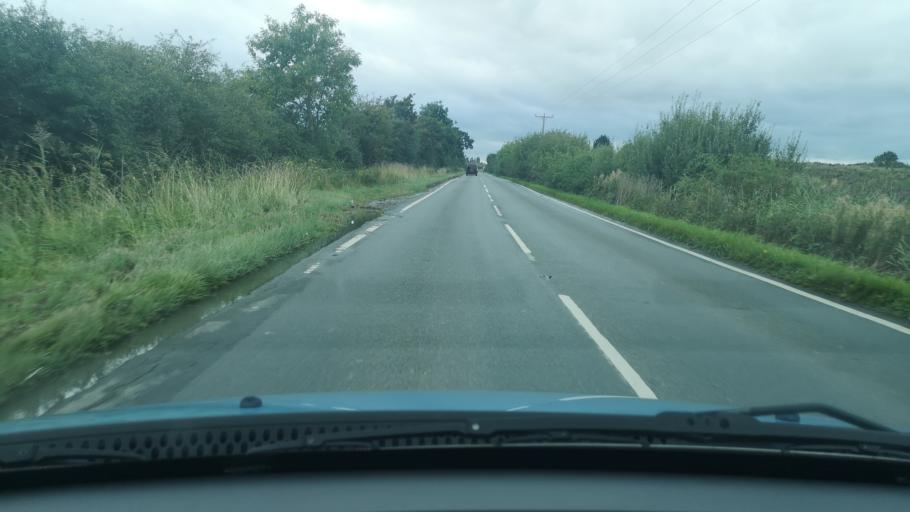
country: GB
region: England
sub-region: Doncaster
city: Hatfield
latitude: 53.6001
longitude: -0.9981
